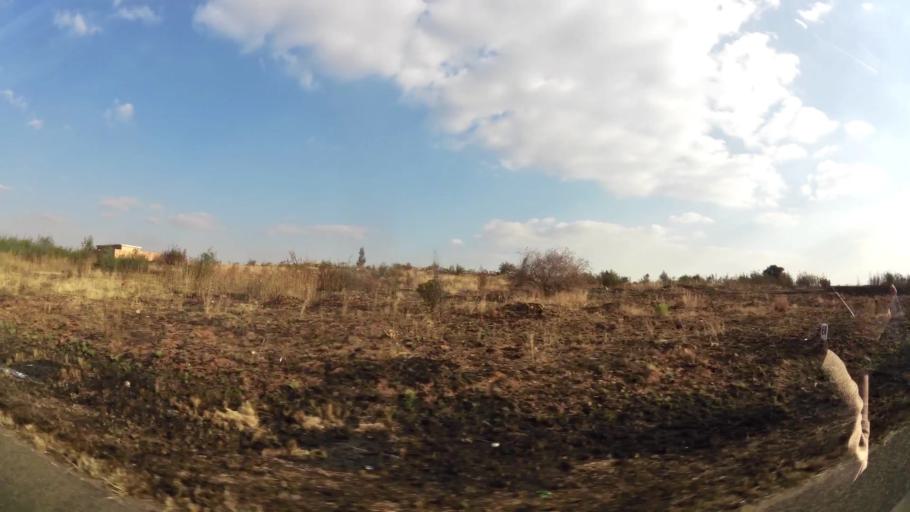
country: ZA
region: Gauteng
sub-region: West Rand District Municipality
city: Krugersdorp
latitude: -26.0990
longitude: 27.7358
